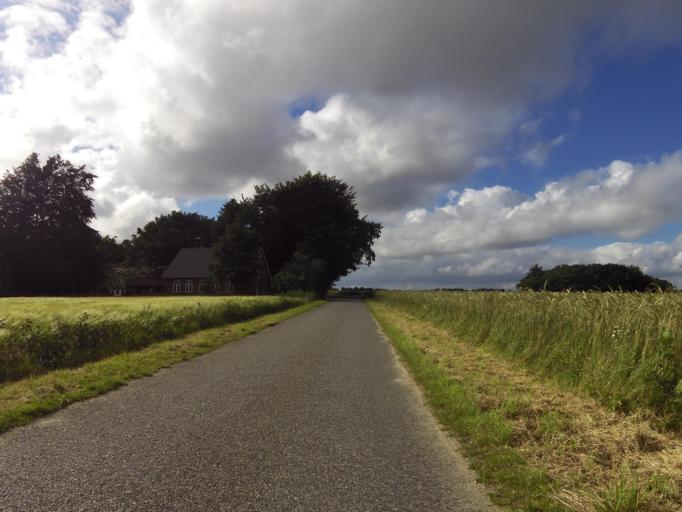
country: DK
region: South Denmark
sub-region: Tonder Kommune
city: Toftlund
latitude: 55.1302
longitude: 9.0769
